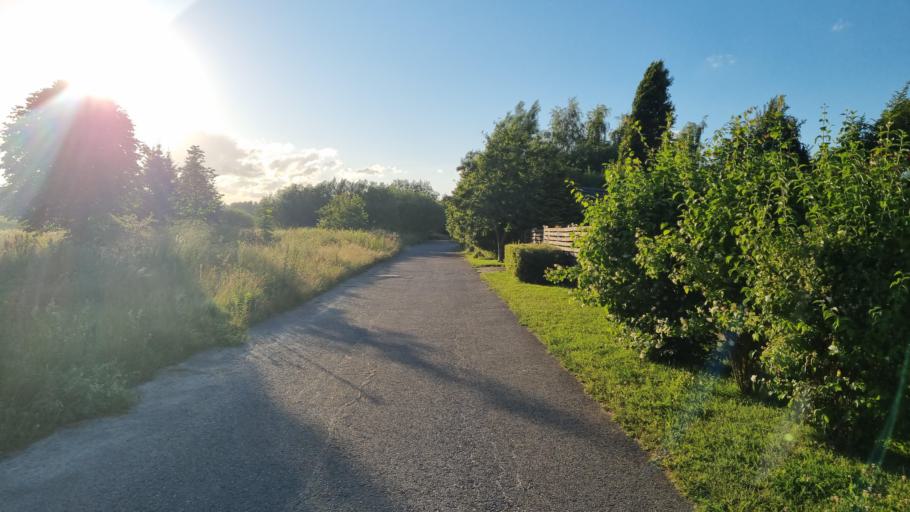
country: LV
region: Kekava
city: Balozi
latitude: 56.8905
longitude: 24.1644
